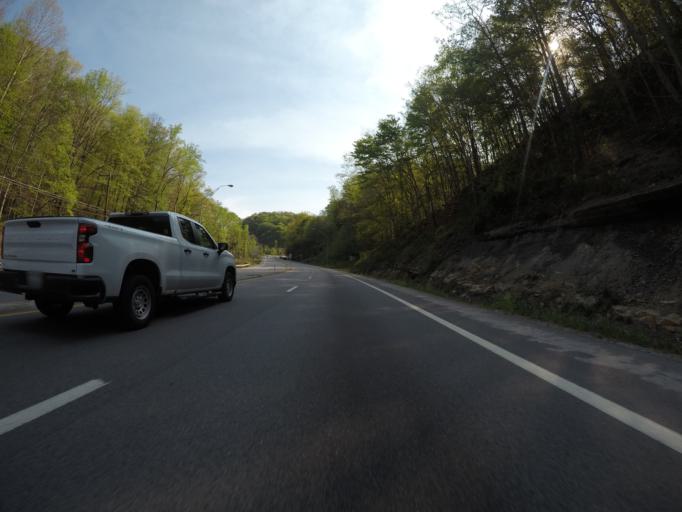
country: US
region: West Virginia
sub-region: Kanawha County
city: Charleston
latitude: 38.3555
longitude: -81.5971
